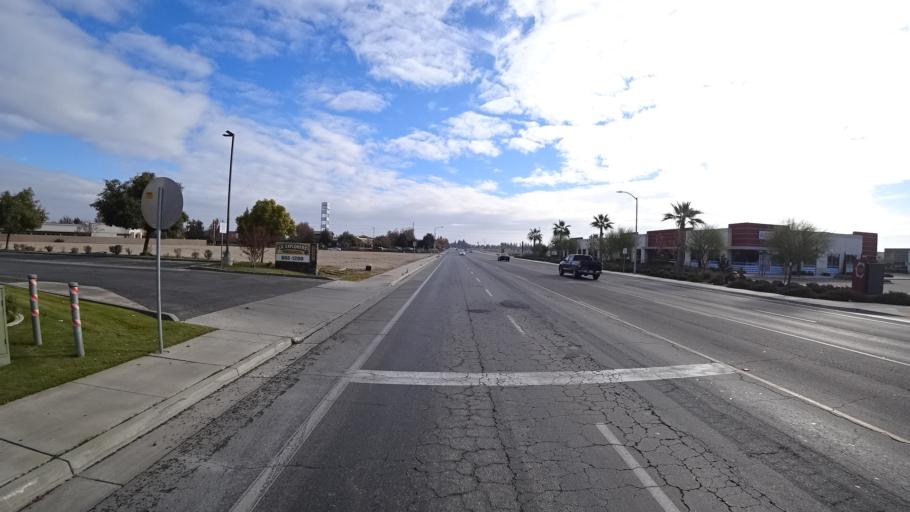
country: US
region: California
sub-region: Kern County
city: Greenacres
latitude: 35.3035
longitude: -119.1000
